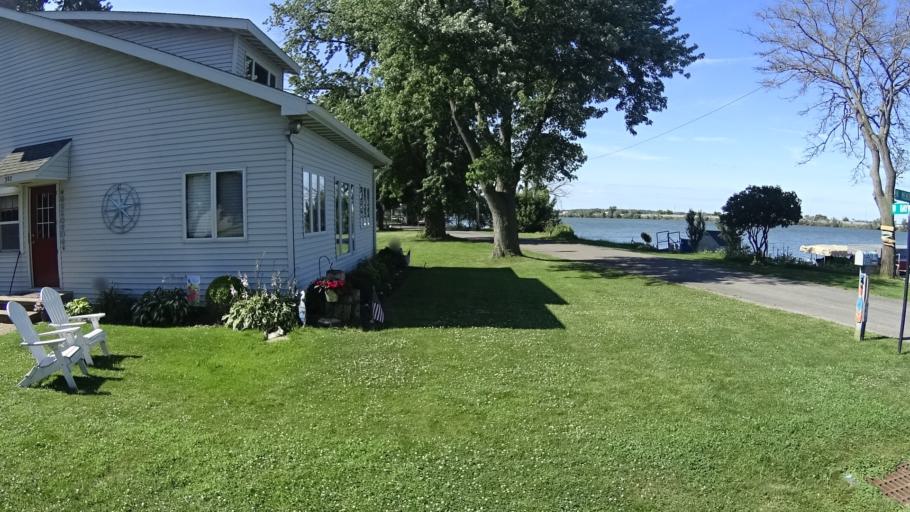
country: US
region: Ohio
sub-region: Ottawa County
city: Port Clinton
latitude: 41.4706
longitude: -82.8291
